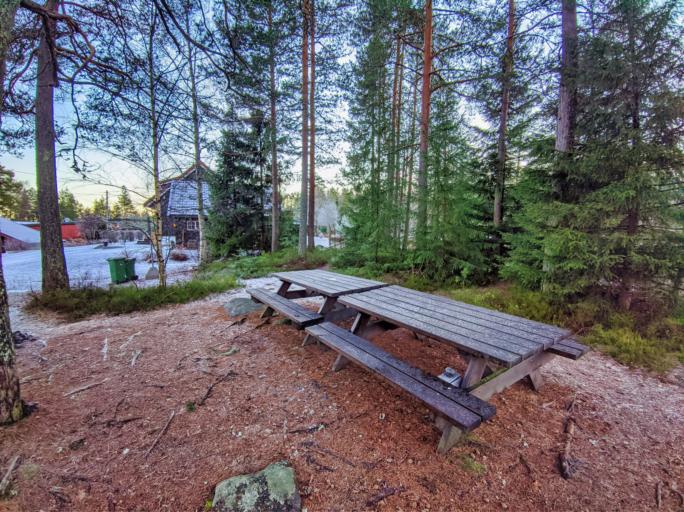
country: NO
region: Akershus
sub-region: Nannestad
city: Teigebyen
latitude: 60.1716
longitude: 10.9821
